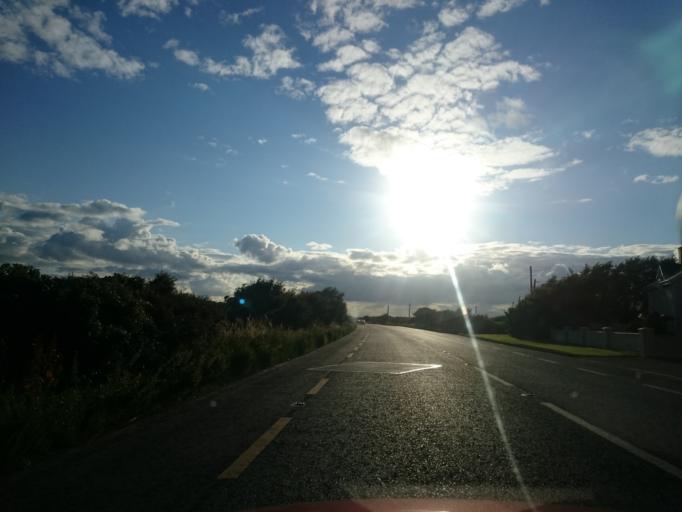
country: IE
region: Leinster
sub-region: Loch Garman
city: Ballygerry
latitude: 52.2446
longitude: -6.3686
